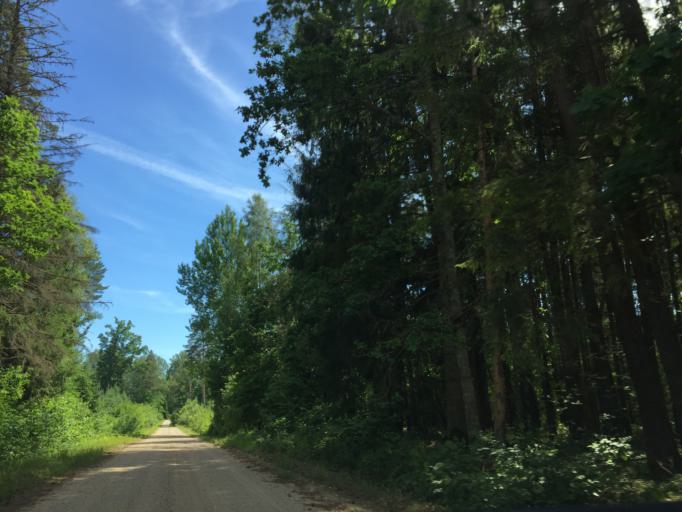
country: LV
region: Kuldigas Rajons
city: Kuldiga
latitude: 57.1207
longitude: 21.8702
